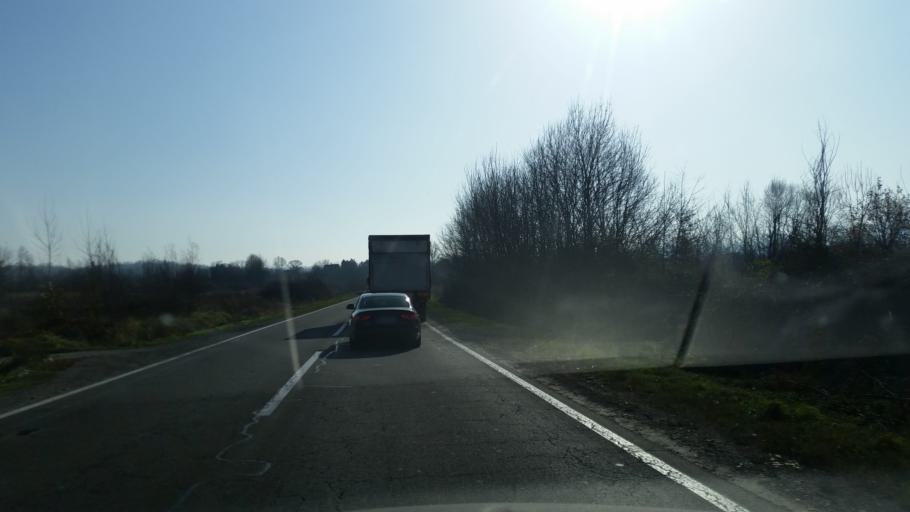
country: RS
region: Central Serbia
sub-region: Kolubarski Okrug
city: Ljig
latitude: 44.2812
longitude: 20.2779
